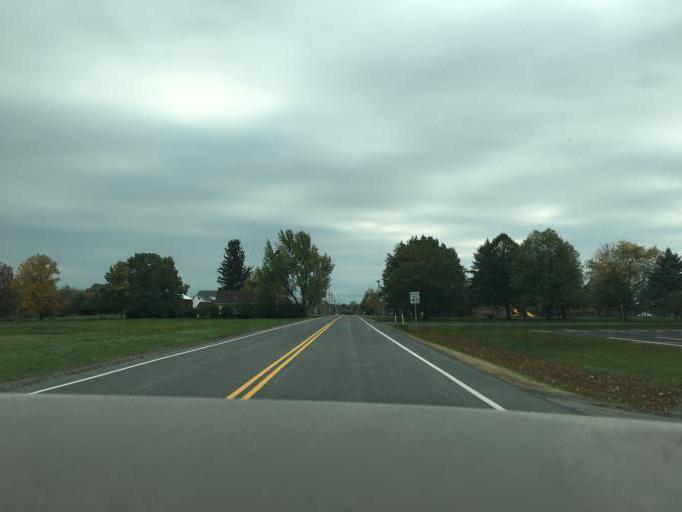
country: US
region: New York
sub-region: Ontario County
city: Victor
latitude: 42.9890
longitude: -77.3262
